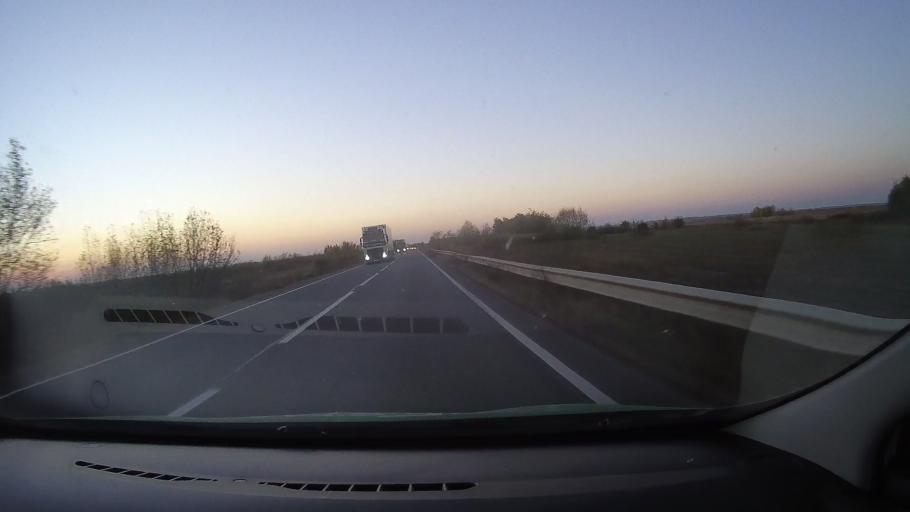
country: RO
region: Bihor
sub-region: Comuna Tarcea
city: Tarcea
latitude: 47.4352
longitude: 22.2020
